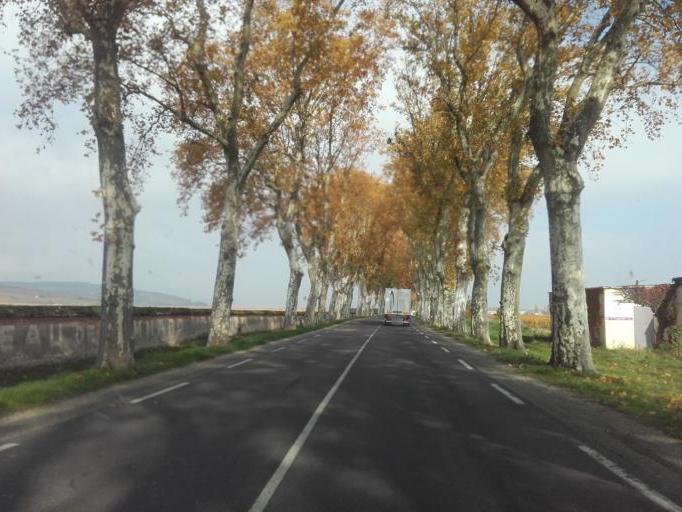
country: FR
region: Bourgogne
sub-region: Departement de la Cote-d'Or
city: Bligny-les-Beaune
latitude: 47.0058
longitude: 4.8049
